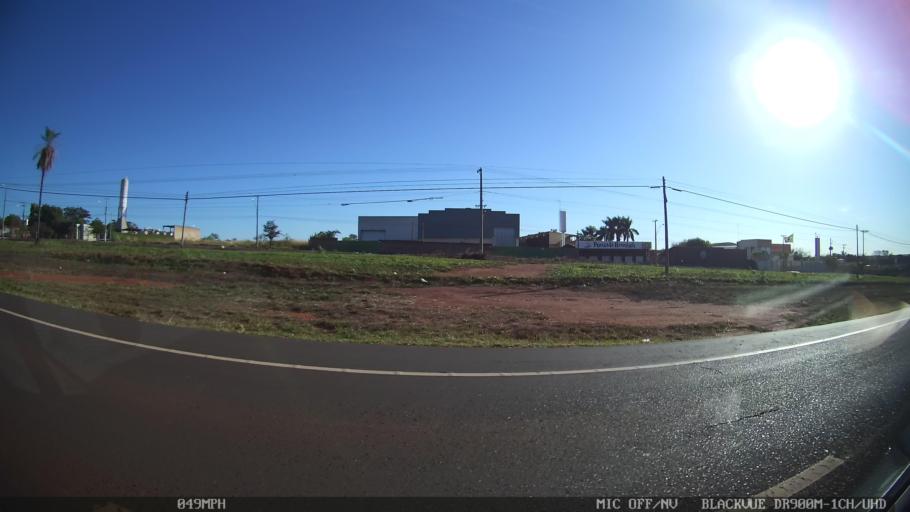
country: BR
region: Sao Paulo
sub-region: Olimpia
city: Olimpia
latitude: -20.6954
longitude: -48.9159
